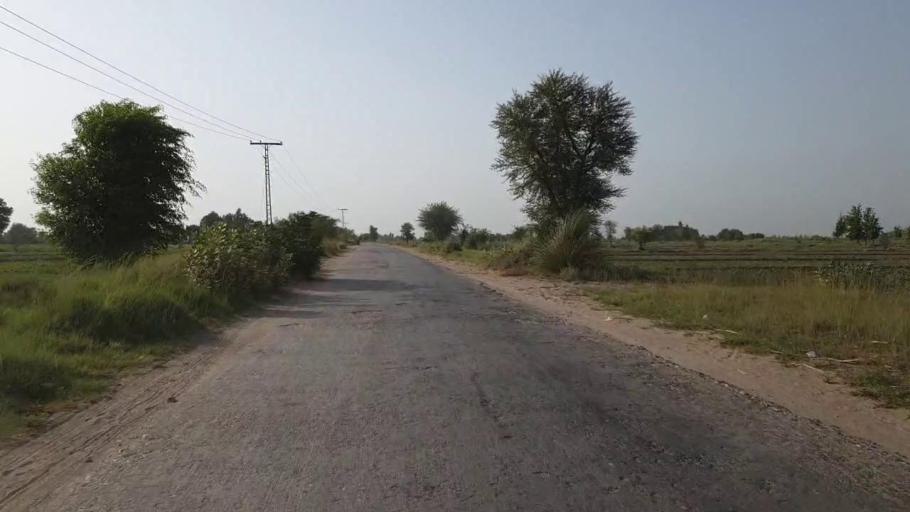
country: PK
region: Sindh
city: Jam Sahib
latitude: 26.3835
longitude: 68.8845
